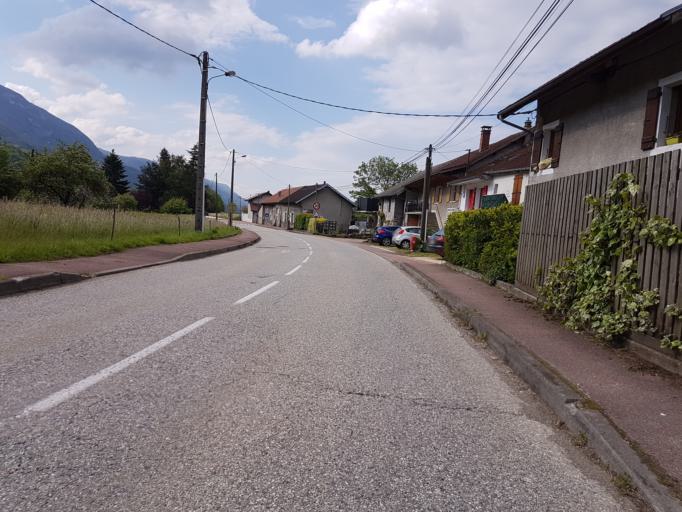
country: FR
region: Rhone-Alpes
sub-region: Departement de la Haute-Savoie
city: Versonnex
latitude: 45.9261
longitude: 5.8341
